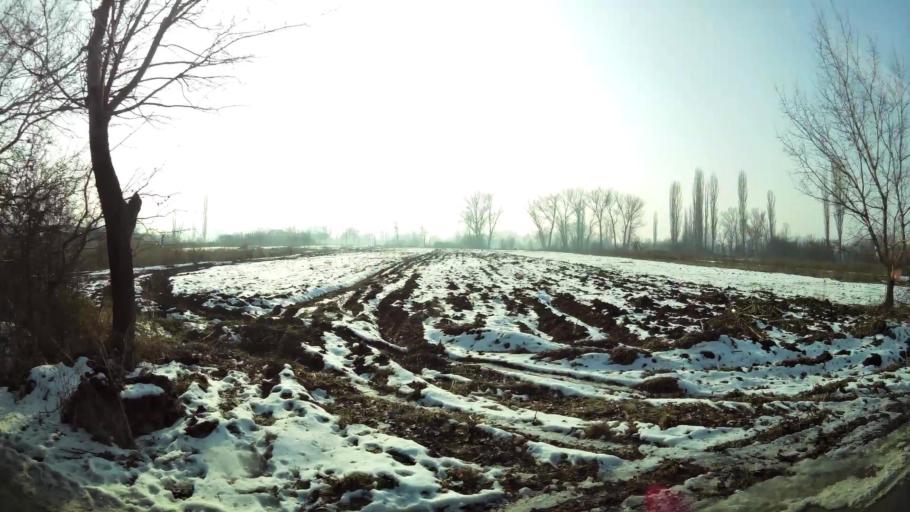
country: MK
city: Kadino
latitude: 41.9646
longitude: 21.5941
